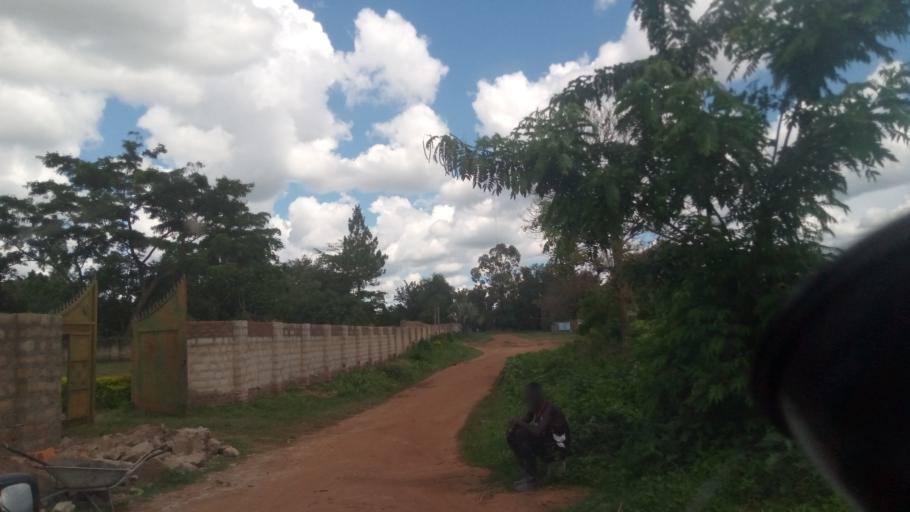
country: UG
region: Northern Region
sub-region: Lira District
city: Lira
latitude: 2.2403
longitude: 32.9021
